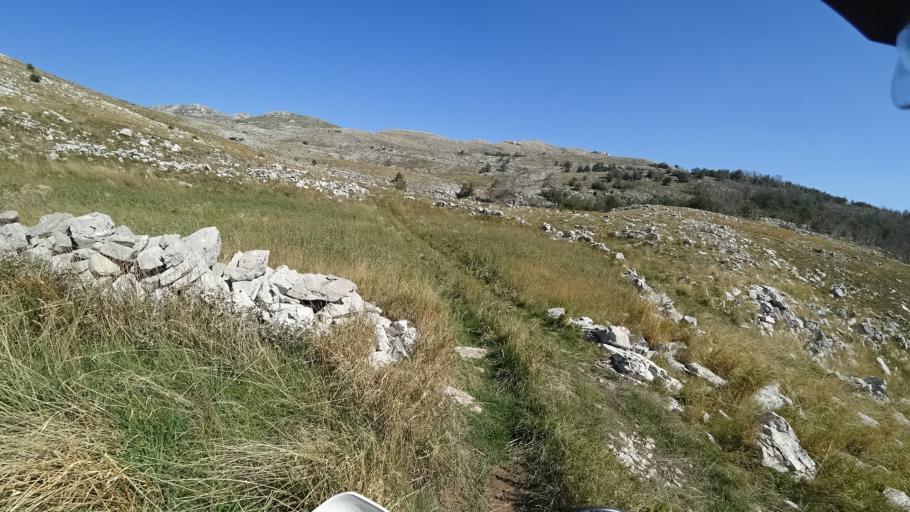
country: HR
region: Splitsko-Dalmatinska
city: Hrvace
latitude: 43.9188
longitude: 16.6052
